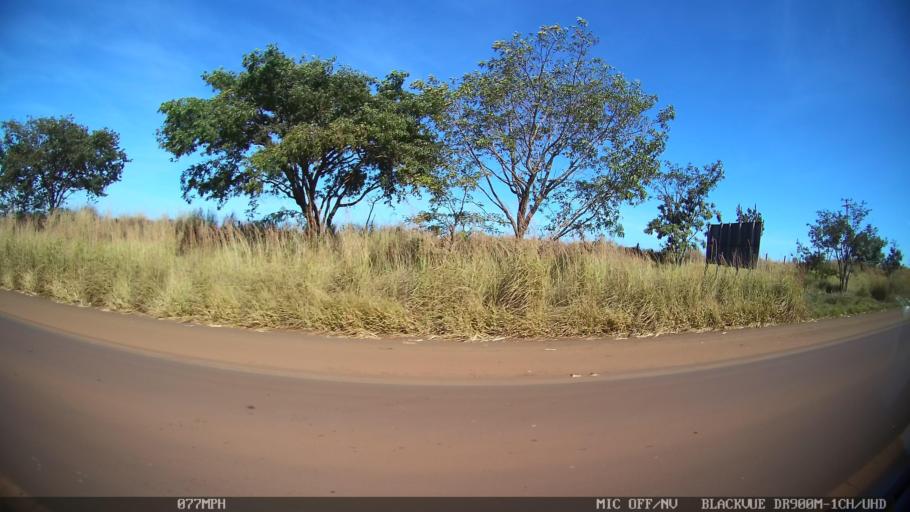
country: BR
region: Sao Paulo
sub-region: Sao Joaquim Da Barra
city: Sao Joaquim da Barra
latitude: -20.5594
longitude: -47.6978
